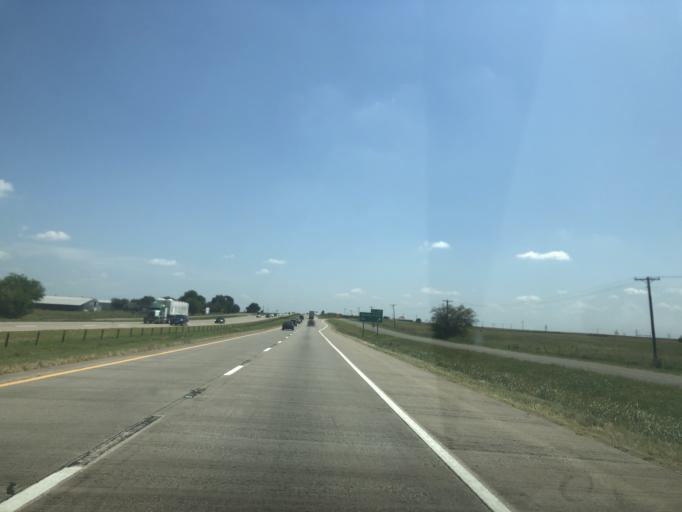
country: US
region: Texas
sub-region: Cooke County
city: Gainesville
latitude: 33.5554
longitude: -97.1663
